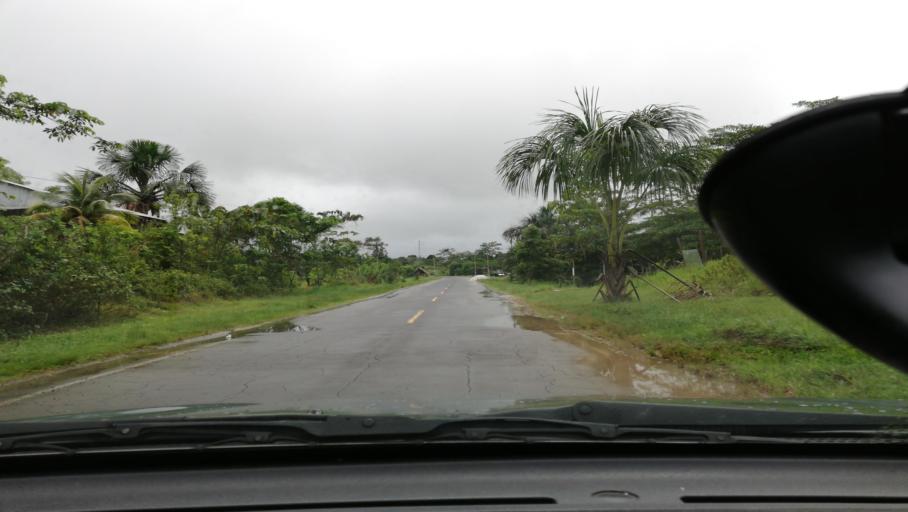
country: PE
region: Loreto
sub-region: Provincia de Loreto
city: Nauta
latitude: -4.2394
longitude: -73.4885
